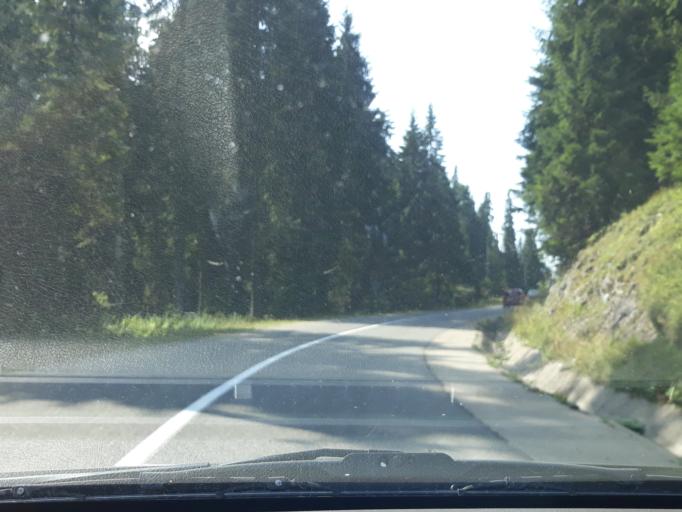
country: RO
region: Alba
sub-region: Comuna Arieseni
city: Arieseni
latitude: 46.5944
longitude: 22.7041
